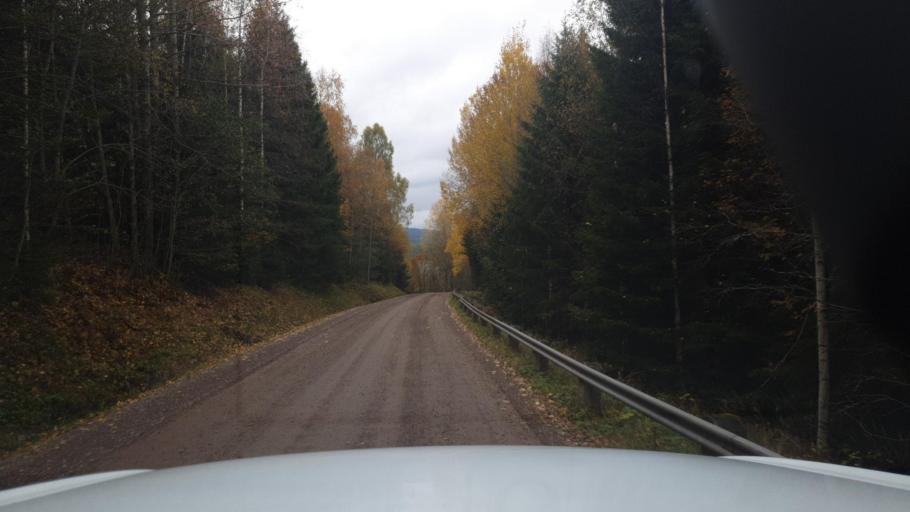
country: SE
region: Vaermland
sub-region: Arvika Kommun
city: Arvika
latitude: 60.0127
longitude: 12.6470
